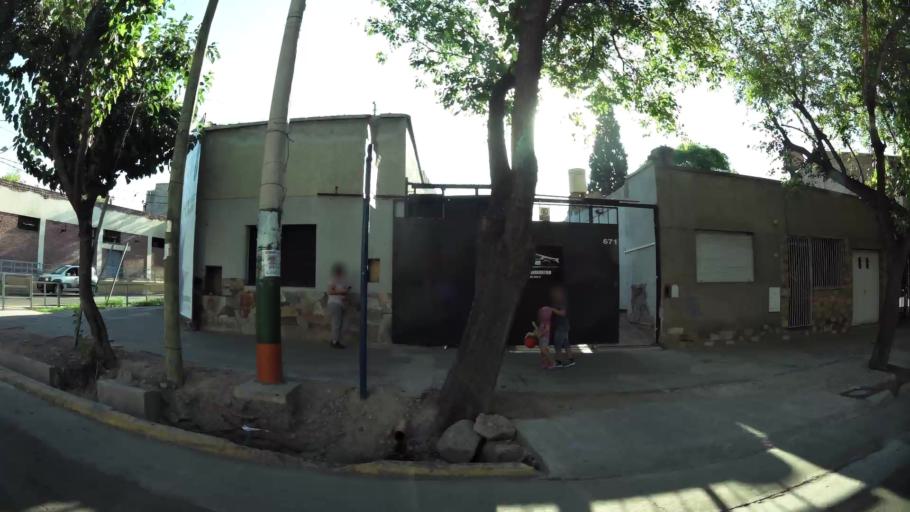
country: AR
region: Mendoza
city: Mendoza
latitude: -32.9032
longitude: -68.8288
